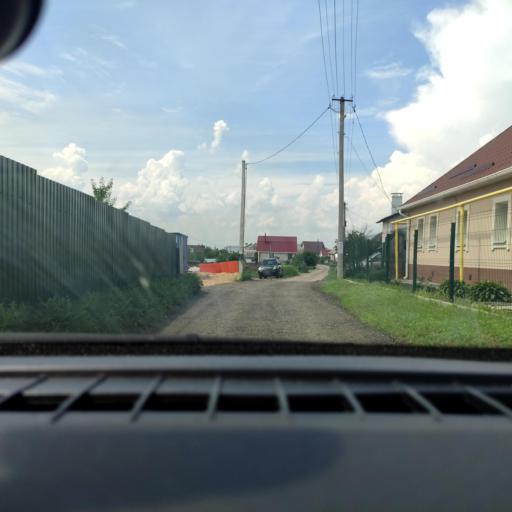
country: RU
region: Voronezj
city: Novaya Usman'
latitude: 51.6791
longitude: 39.3681
